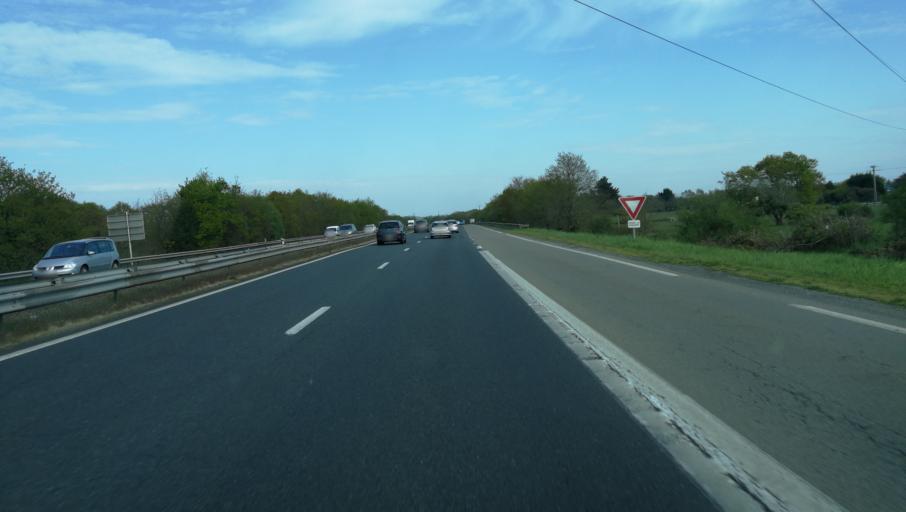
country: FR
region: Pays de la Loire
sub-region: Departement de la Loire-Atlantique
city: Prinquiau
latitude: 47.3570
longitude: -2.0003
